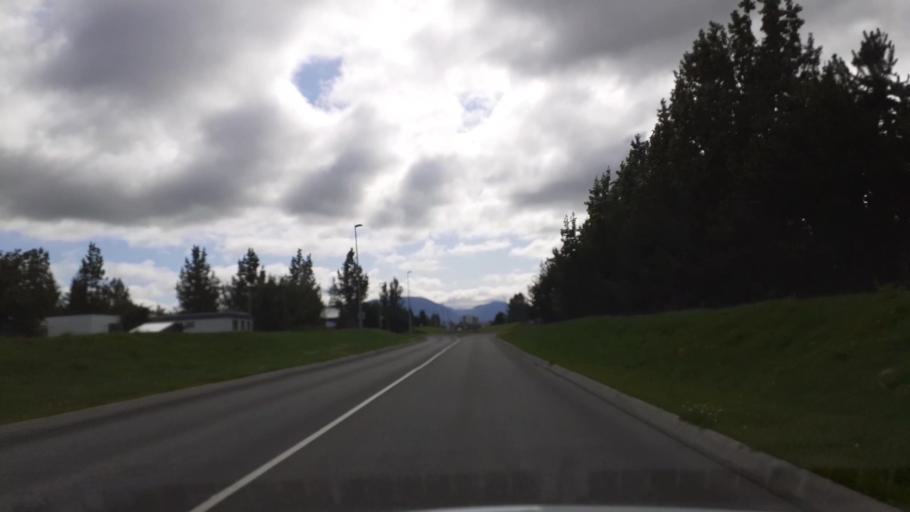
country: IS
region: Northeast
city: Akureyri
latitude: 65.6752
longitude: -18.1100
